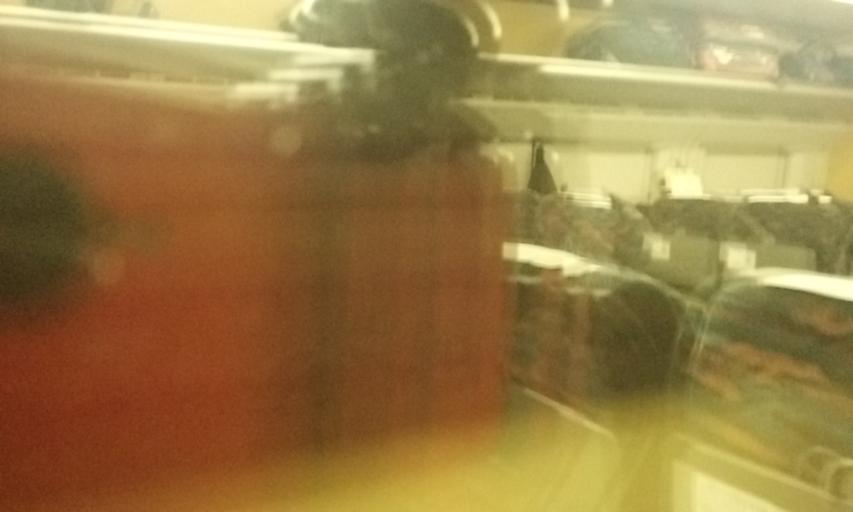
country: JP
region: Tochigi
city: Kuroiso
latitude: 36.9860
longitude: 140.0735
